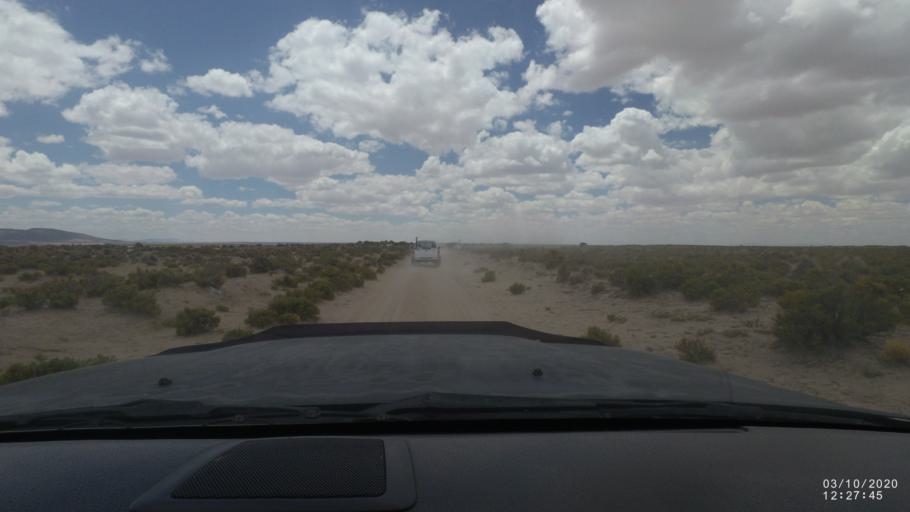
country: BO
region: Oruro
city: Poopo
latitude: -18.6922
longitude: -67.5545
